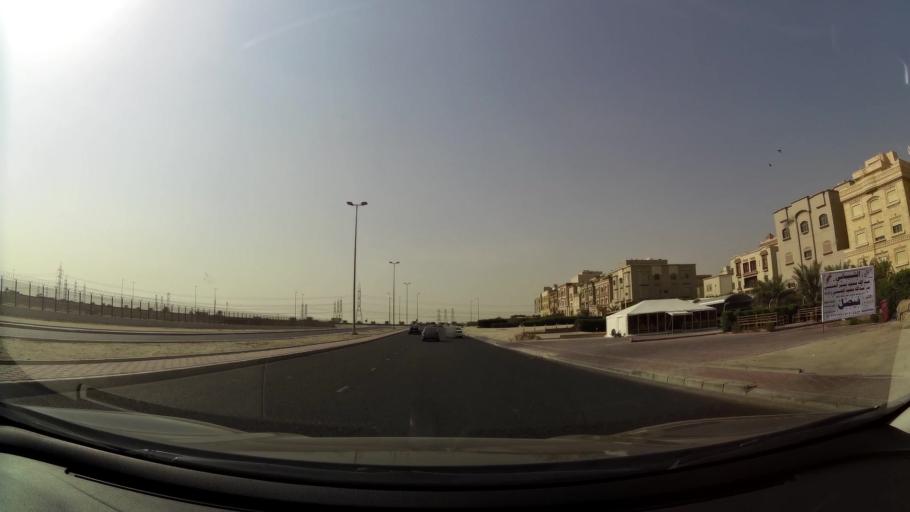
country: KW
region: Al Ahmadi
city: Ar Riqqah
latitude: 29.1228
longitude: 48.0958
